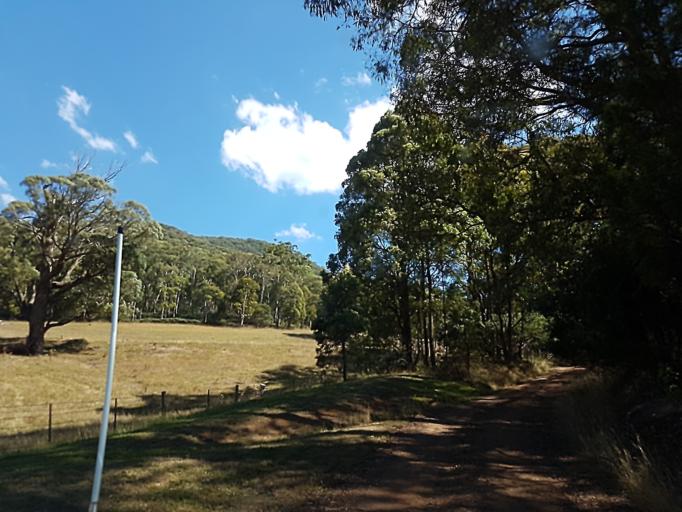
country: AU
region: Victoria
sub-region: Alpine
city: Mount Beauty
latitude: -36.8743
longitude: 147.0571
